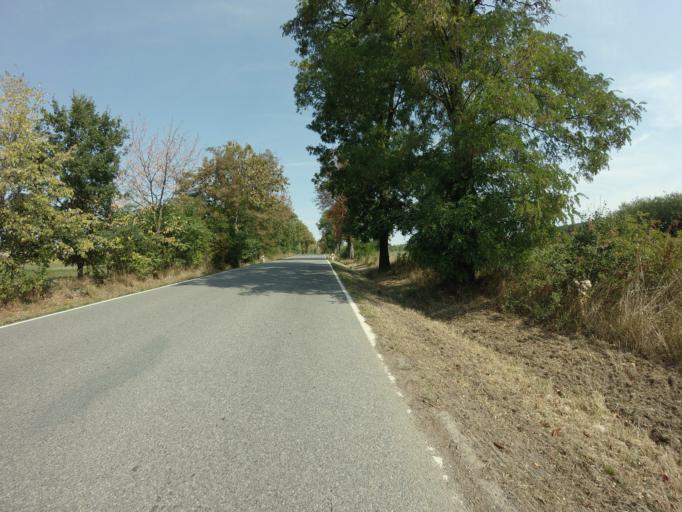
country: CZ
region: Central Bohemia
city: Petrovice
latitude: 49.6038
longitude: 14.3840
